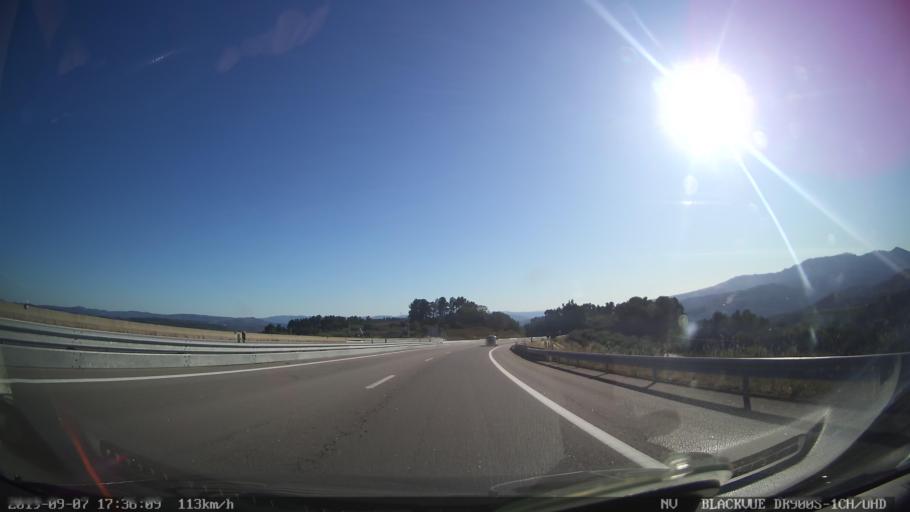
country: PT
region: Vila Real
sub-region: Vila Real
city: Vila Real
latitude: 41.2455
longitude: -7.7188
